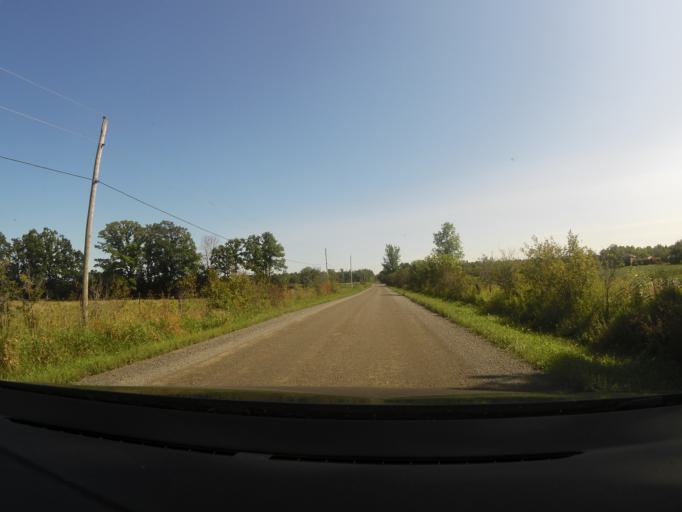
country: CA
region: Ontario
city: Carleton Place
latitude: 45.3286
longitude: -76.0860
